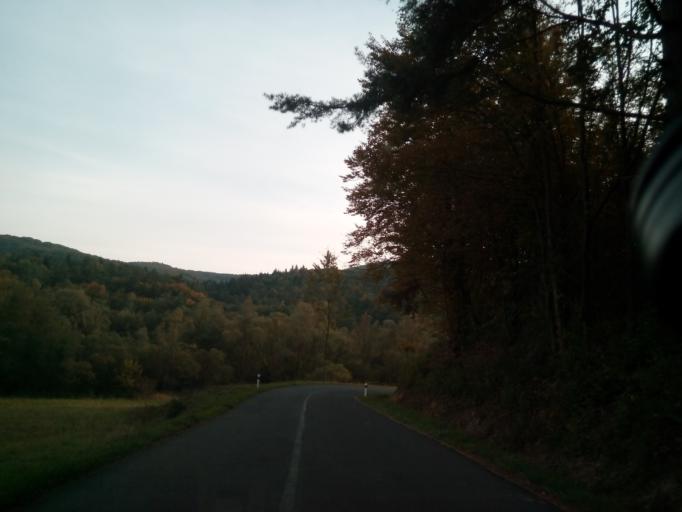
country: SK
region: Presovsky
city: Svidnik
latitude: 49.3533
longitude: 21.4647
